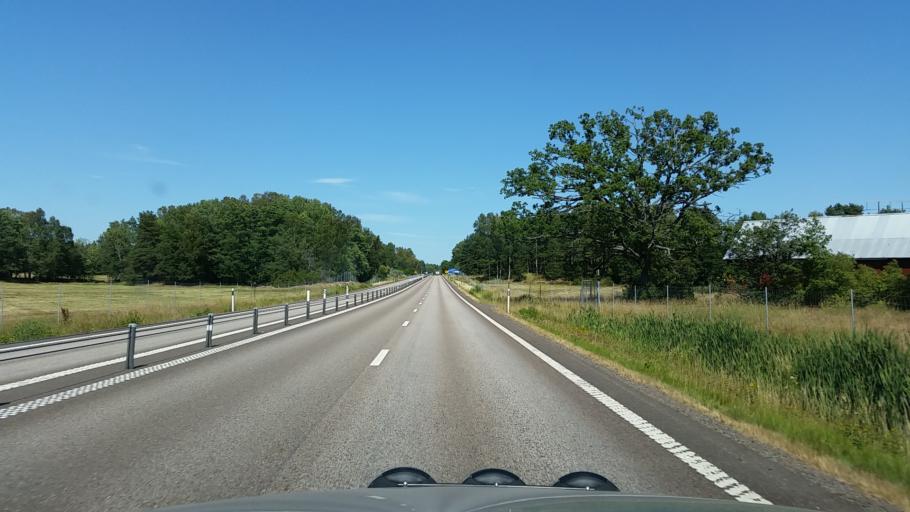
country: SE
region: Vaestra Goetaland
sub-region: Melleruds Kommun
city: Mellerud
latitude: 58.8366
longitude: 12.5395
